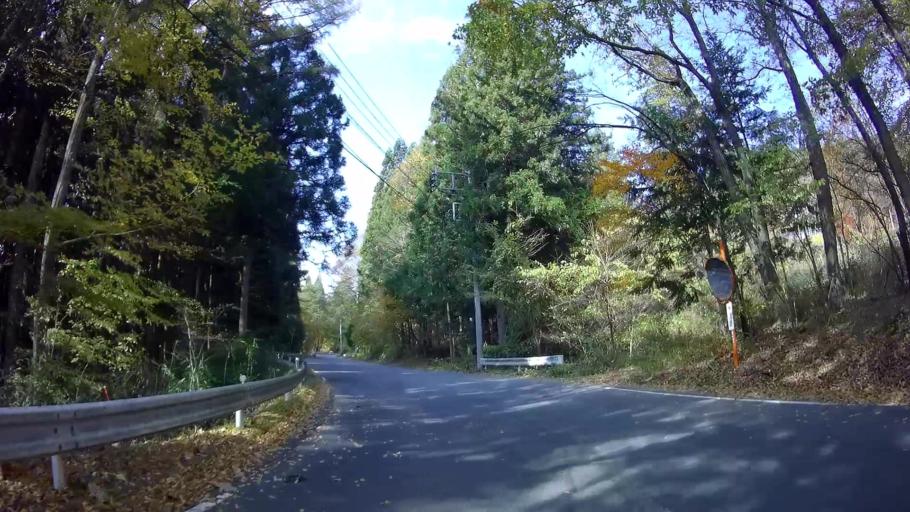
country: JP
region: Gunma
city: Nakanojomachi
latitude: 36.5065
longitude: 138.6775
